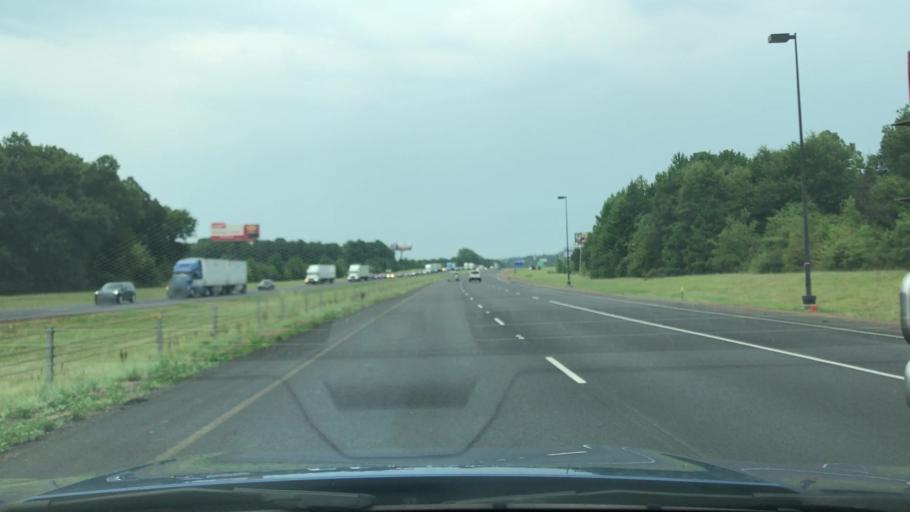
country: US
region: Louisiana
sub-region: Caddo Parish
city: Greenwood
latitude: 32.4511
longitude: -93.9964
